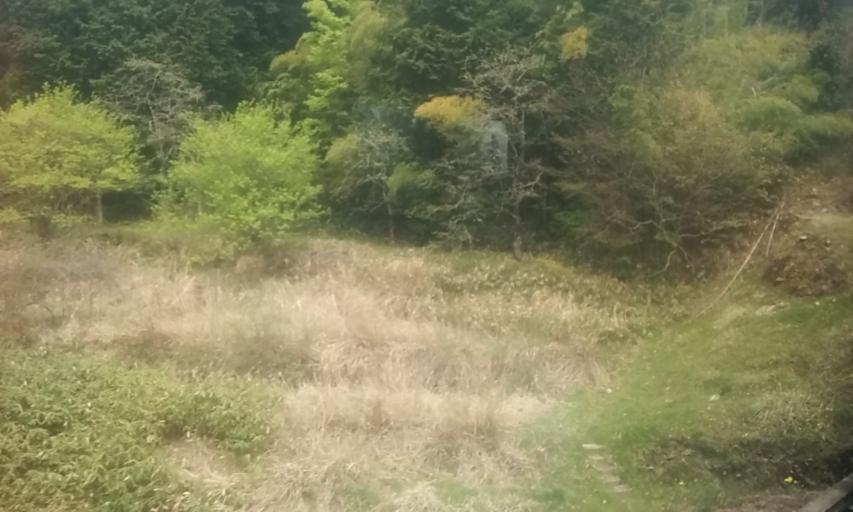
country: JP
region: Gifu
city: Tarui
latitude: 35.3542
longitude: 136.4445
